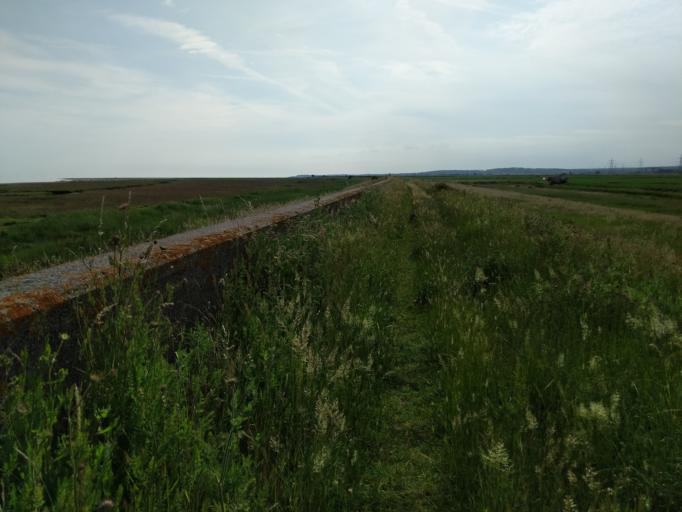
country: GB
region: England
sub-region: Kent
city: Faversham
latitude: 51.3433
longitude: 0.9152
